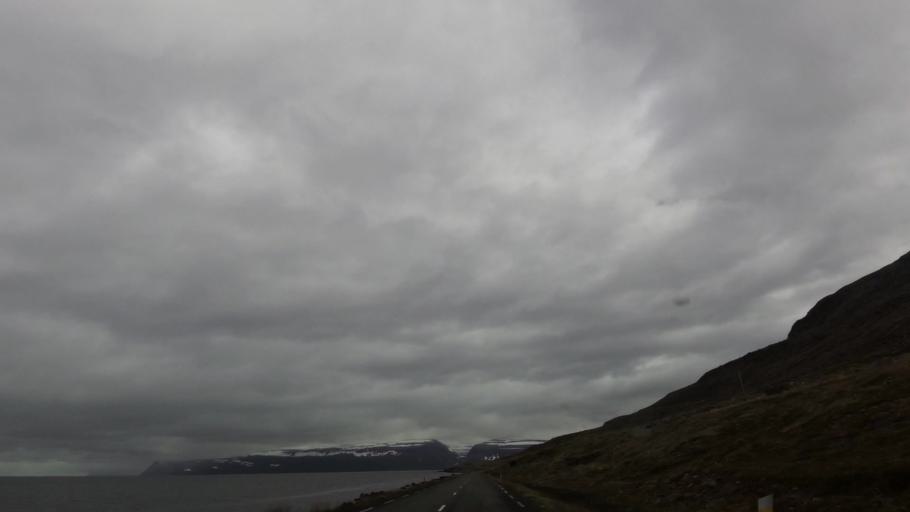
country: IS
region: Westfjords
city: Isafjoerdur
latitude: 66.0350
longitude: -22.7738
